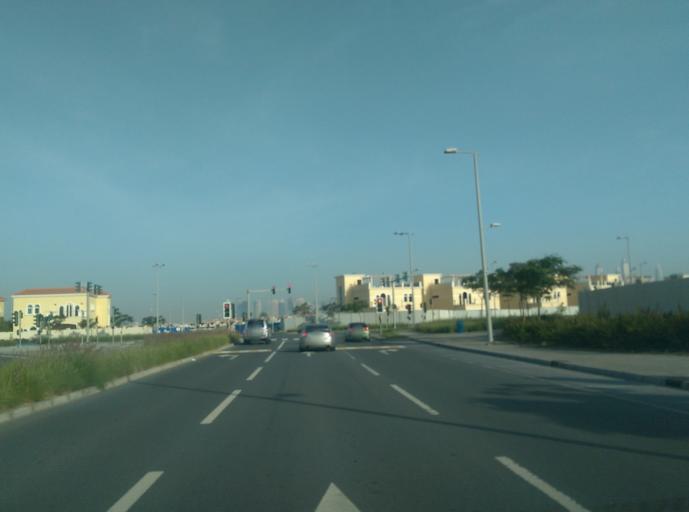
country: AE
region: Dubai
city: Dubai
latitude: 25.0432
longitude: 55.1683
